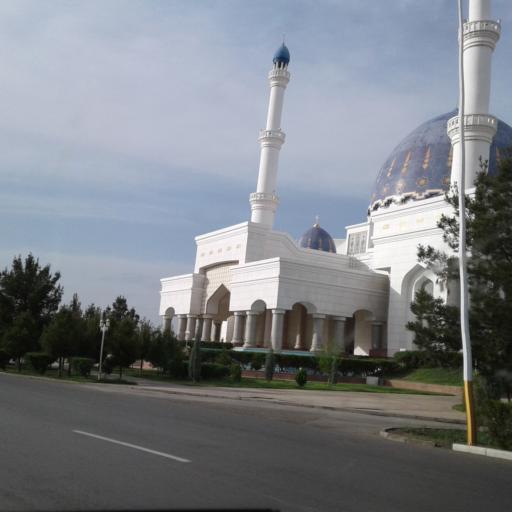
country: TM
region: Mary
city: Mary
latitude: 37.5885
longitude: 61.8522
